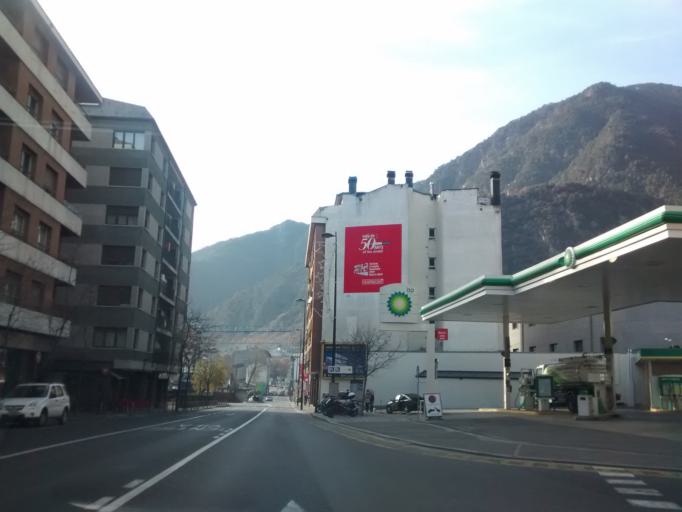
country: AD
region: Andorra la Vella
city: Andorra la Vella
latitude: 42.4974
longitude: 1.5025
